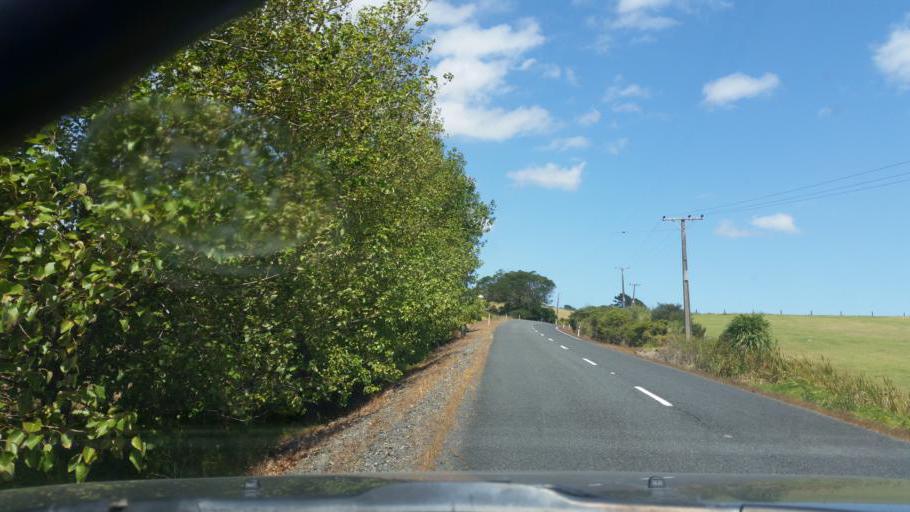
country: NZ
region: Northland
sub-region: Kaipara District
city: Dargaville
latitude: -35.9072
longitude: 173.8442
